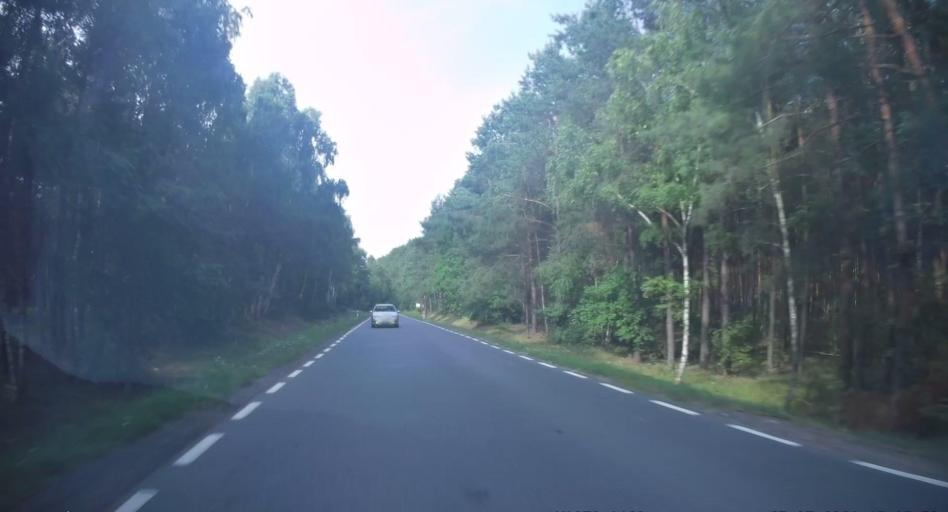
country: PL
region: Lodz Voivodeship
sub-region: Powiat tomaszowski
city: Inowlodz
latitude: 51.5389
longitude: 20.2333
